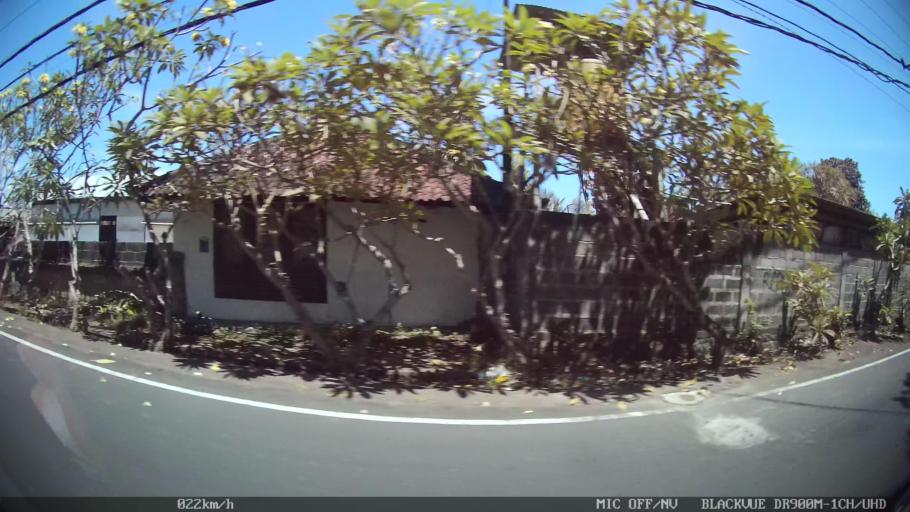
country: ID
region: Bali
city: Klungkung
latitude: -8.5753
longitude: 115.3363
